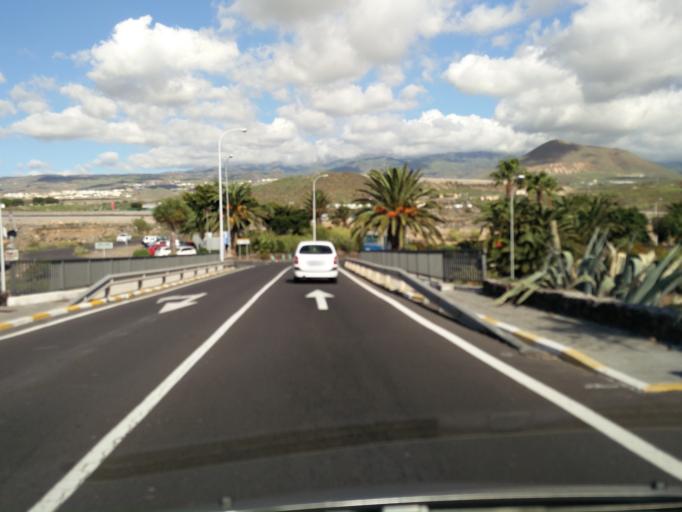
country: ES
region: Canary Islands
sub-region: Provincia de Santa Cruz de Tenerife
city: San Isidro
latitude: 28.0583
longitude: -16.5805
